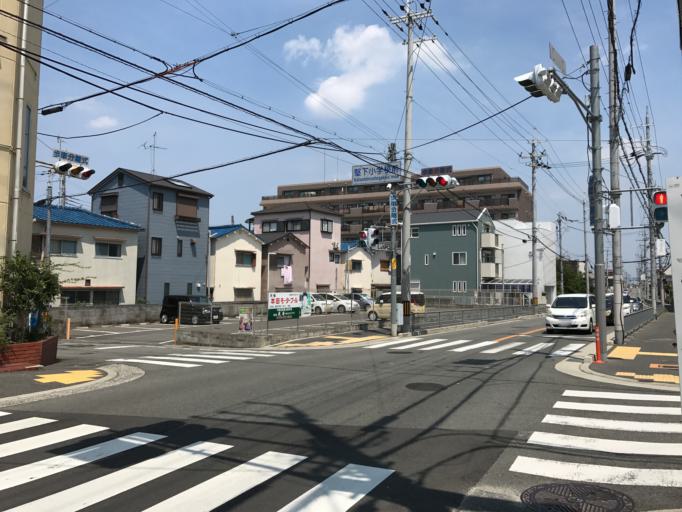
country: JP
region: Osaka
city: Kashihara
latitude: 34.5906
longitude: 135.6311
